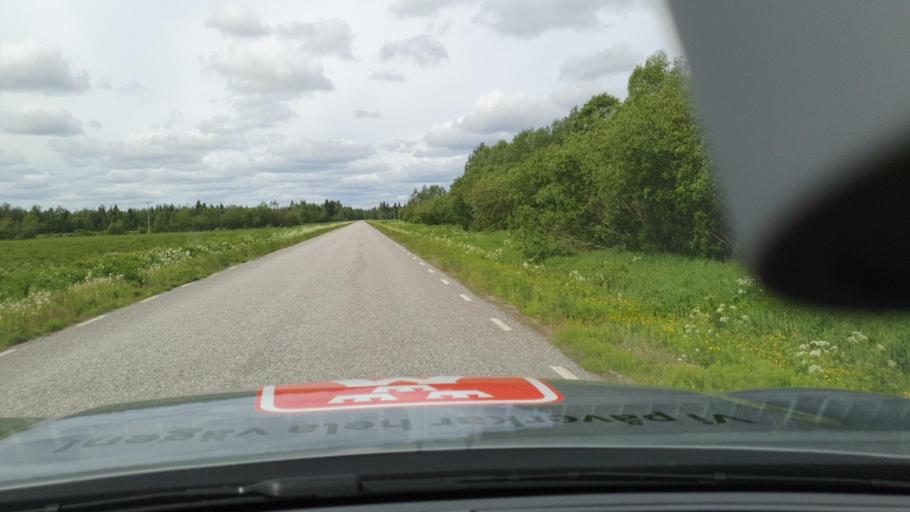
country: FI
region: Lapland
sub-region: Torniolaakso
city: Ylitornio
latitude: 66.0338
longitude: 23.8334
